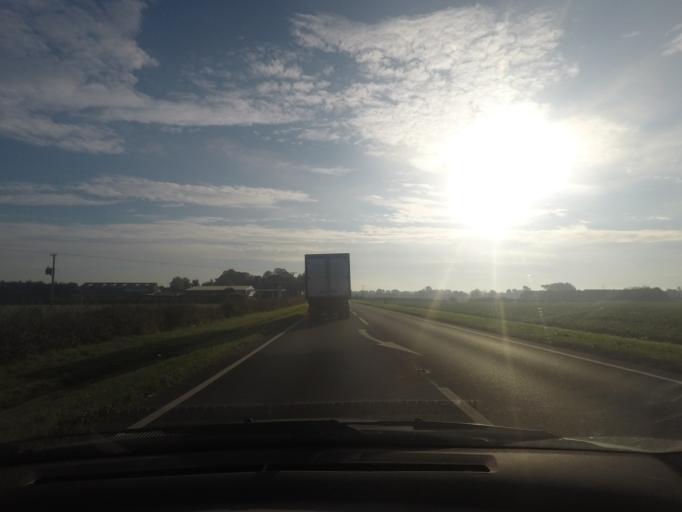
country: GB
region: England
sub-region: East Riding of Yorkshire
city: Londesborough
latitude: 53.8808
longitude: -0.7161
